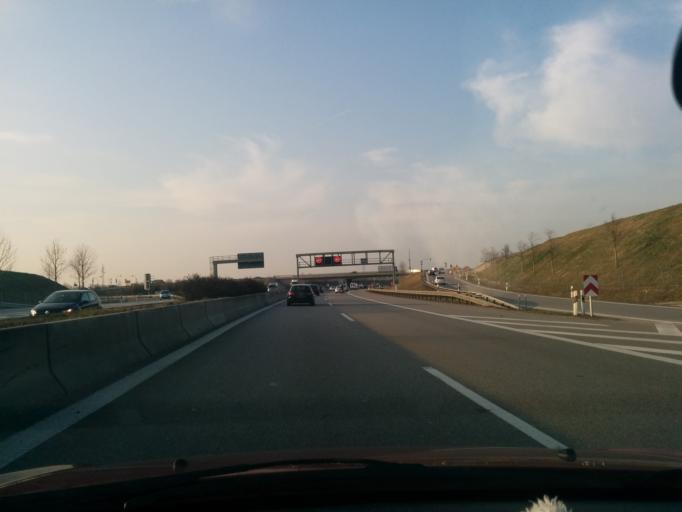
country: DE
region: Bavaria
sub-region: Upper Bavaria
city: Germering
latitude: 48.1437
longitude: 11.3945
